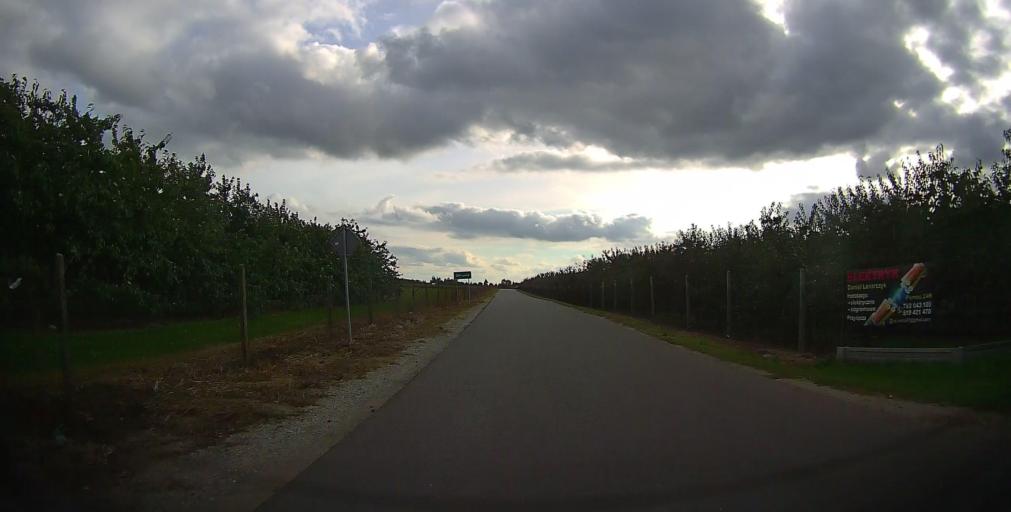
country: PL
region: Masovian Voivodeship
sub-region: Powiat bialobrzeski
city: Promna
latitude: 51.7291
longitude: 20.9633
